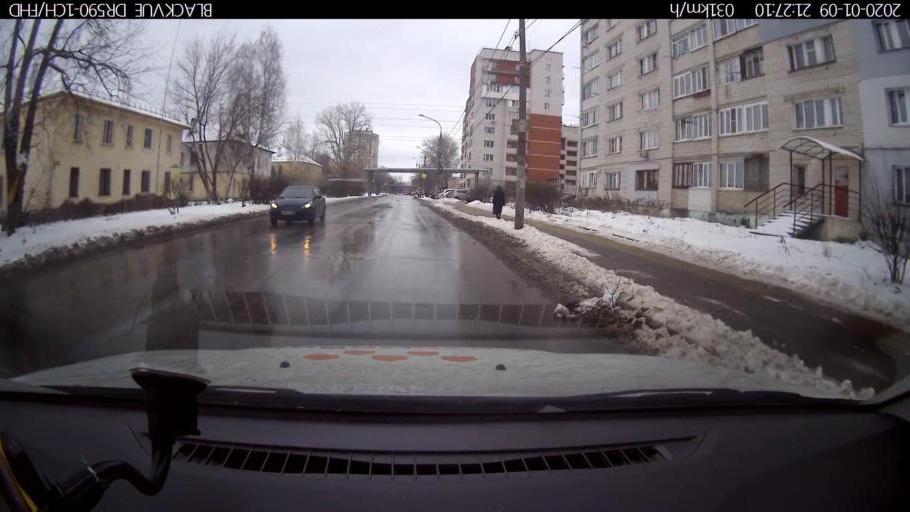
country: RU
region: Nizjnij Novgorod
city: Gorbatovka
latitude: 56.2917
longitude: 43.8463
